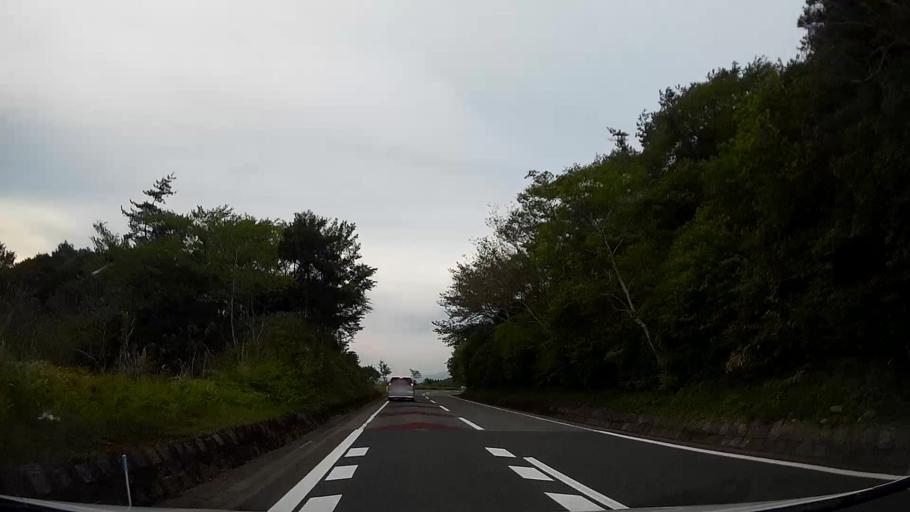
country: JP
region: Shizuoka
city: Atami
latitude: 35.0755
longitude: 139.0267
